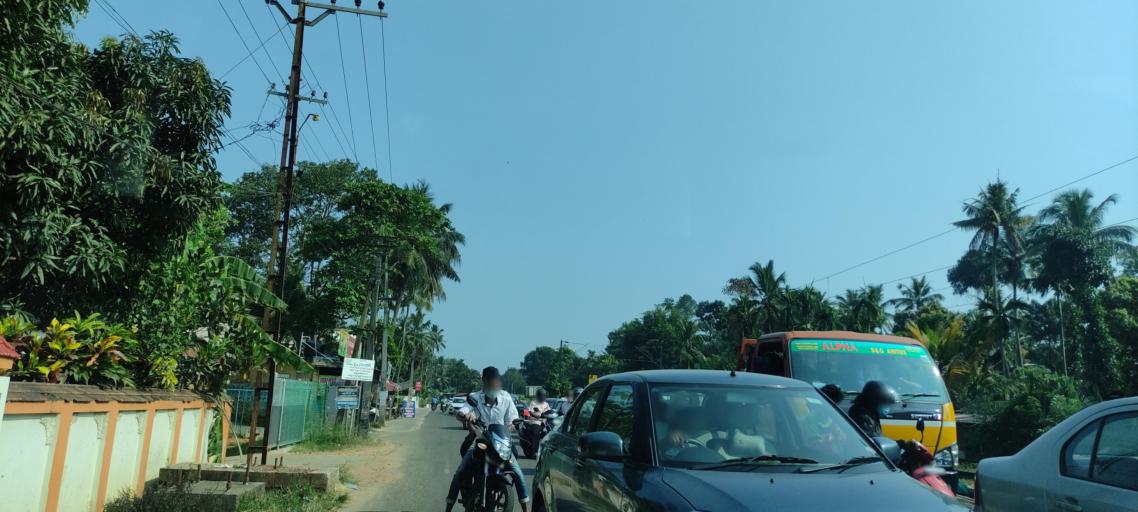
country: IN
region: Kerala
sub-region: Kollam
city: Panmana
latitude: 9.0540
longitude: 76.5562
